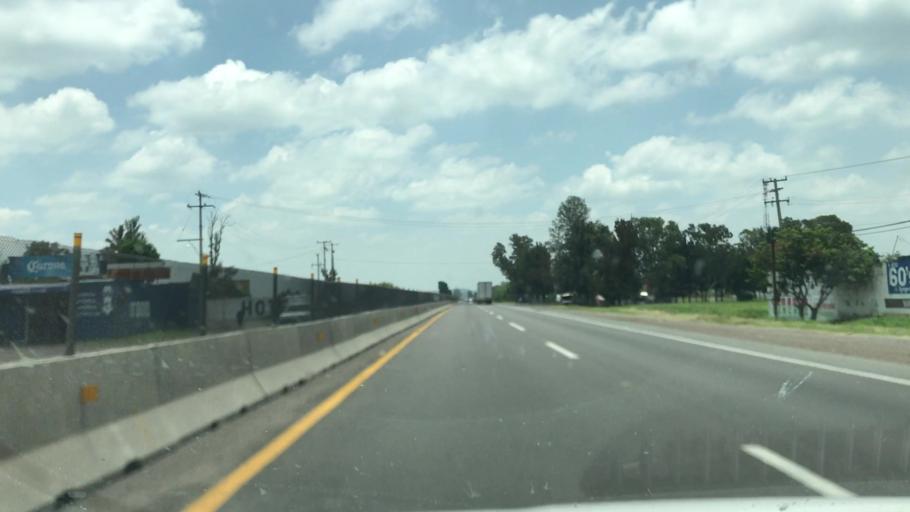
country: MX
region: Guanajuato
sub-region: Abasolo
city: San Bernardo Pena Blanca
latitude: 20.4923
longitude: -101.4862
